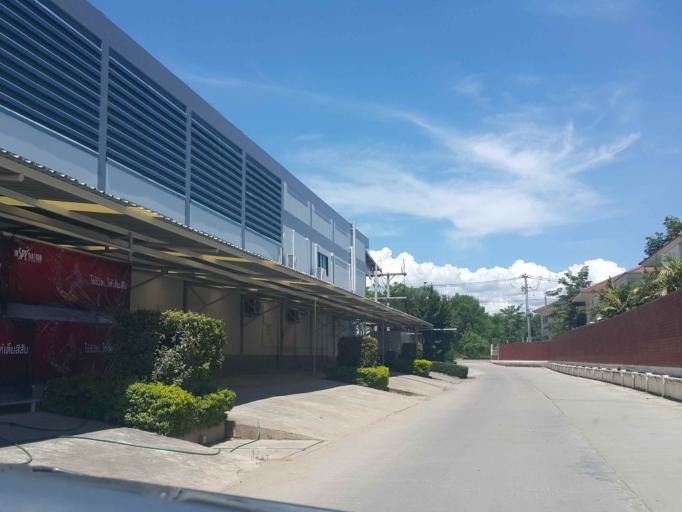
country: TH
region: Chiang Mai
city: Saraphi
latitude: 18.7595
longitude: 99.0364
